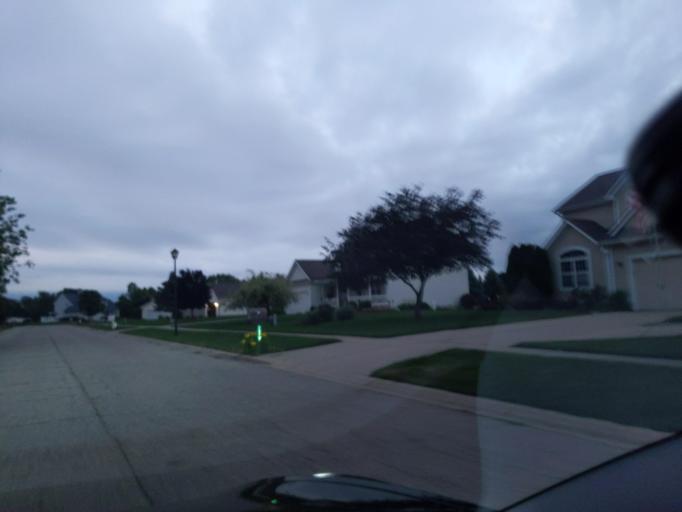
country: US
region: Michigan
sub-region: Eaton County
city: Dimondale
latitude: 42.6532
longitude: -84.5863
